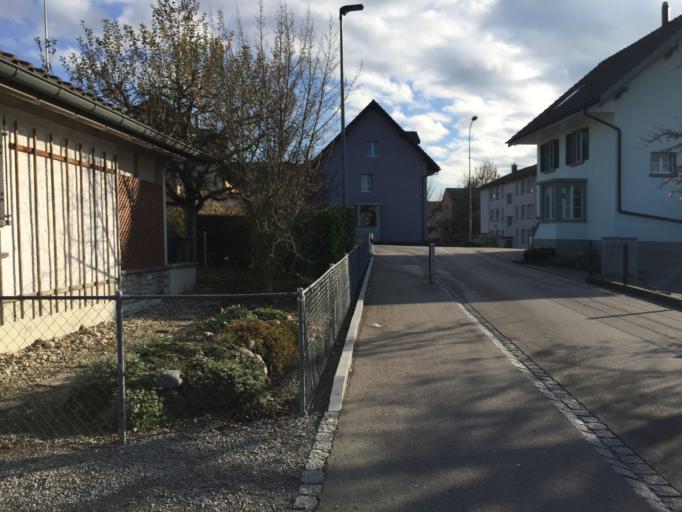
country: CH
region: Bern
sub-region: Bern-Mittelland District
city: Munsingen
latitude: 46.8702
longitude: 7.5570
